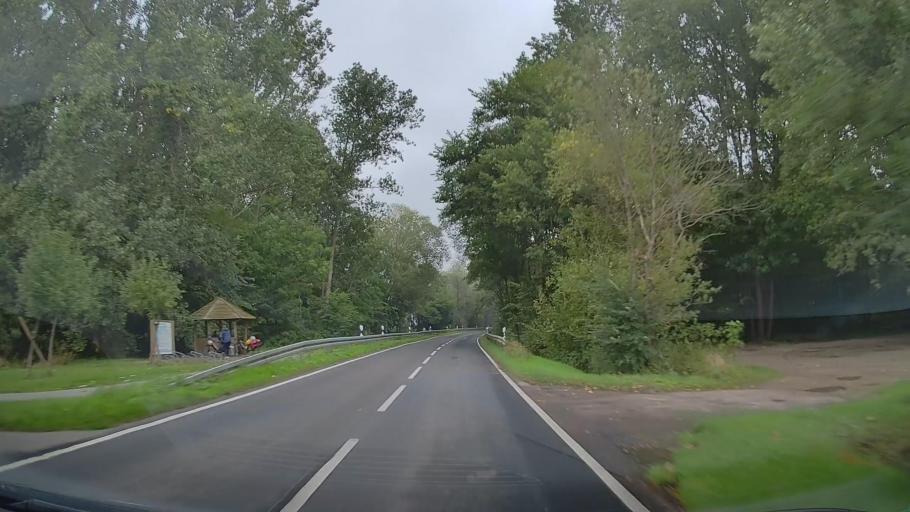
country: DE
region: Mecklenburg-Vorpommern
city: Neubukow
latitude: 54.0871
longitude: 11.6316
